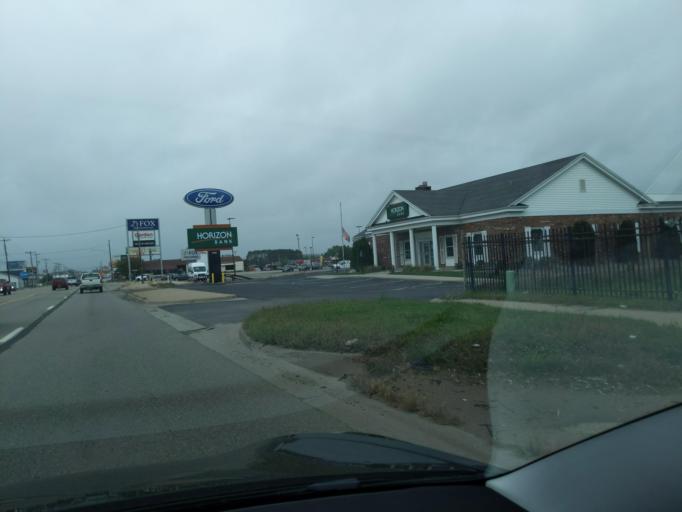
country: US
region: Michigan
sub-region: Wexford County
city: Cadillac
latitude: 44.2704
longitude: -85.4064
